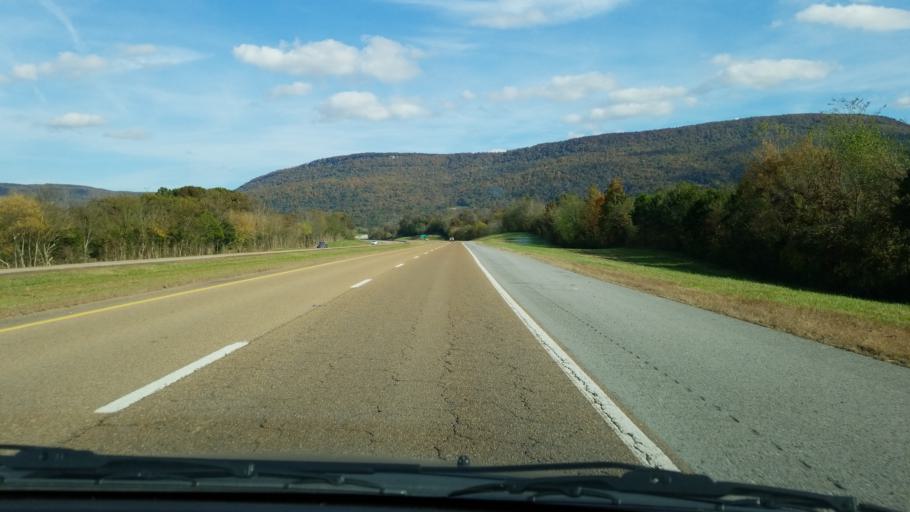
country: US
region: Tennessee
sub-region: Sequatchie County
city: Dunlap
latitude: 35.3930
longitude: -85.3526
